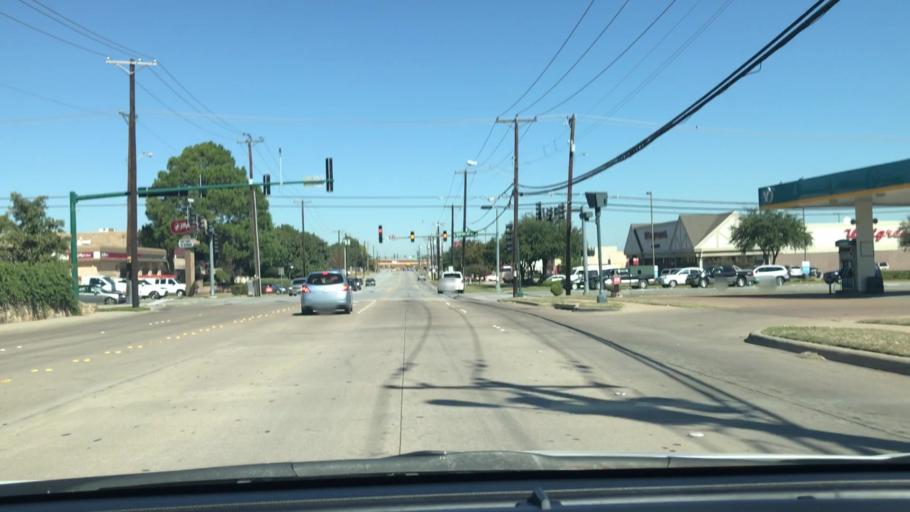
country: US
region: Texas
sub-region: Tarrant County
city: Hurst
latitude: 32.8334
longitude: -97.1863
